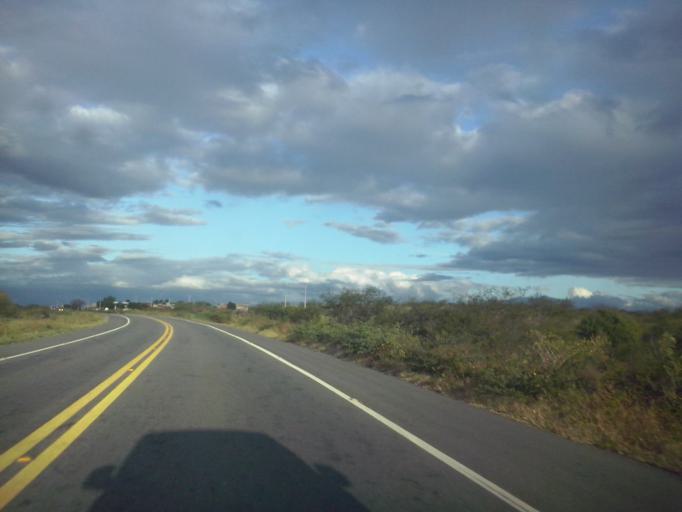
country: BR
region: Paraiba
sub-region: Patos
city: Patos
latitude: -6.9472
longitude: -37.4019
